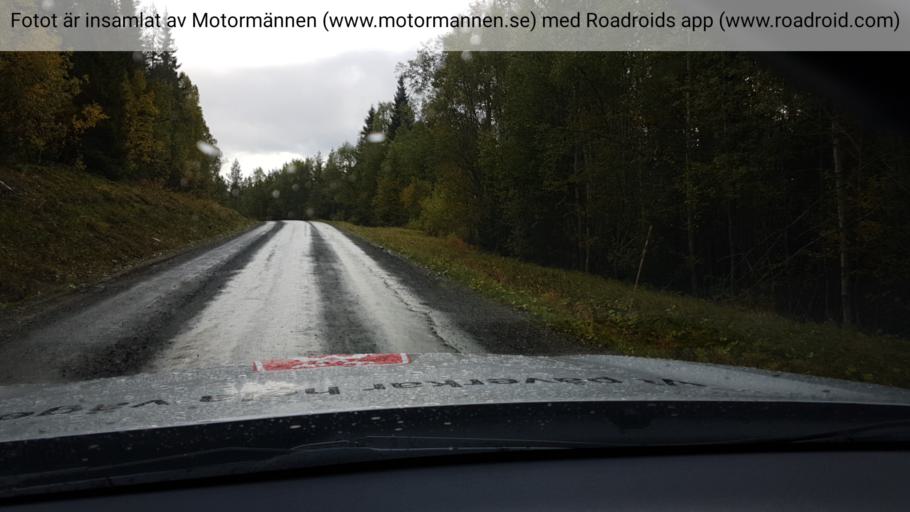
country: SE
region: Jaemtland
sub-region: Krokoms Kommun
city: Valla
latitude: 64.1067
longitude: 14.1506
